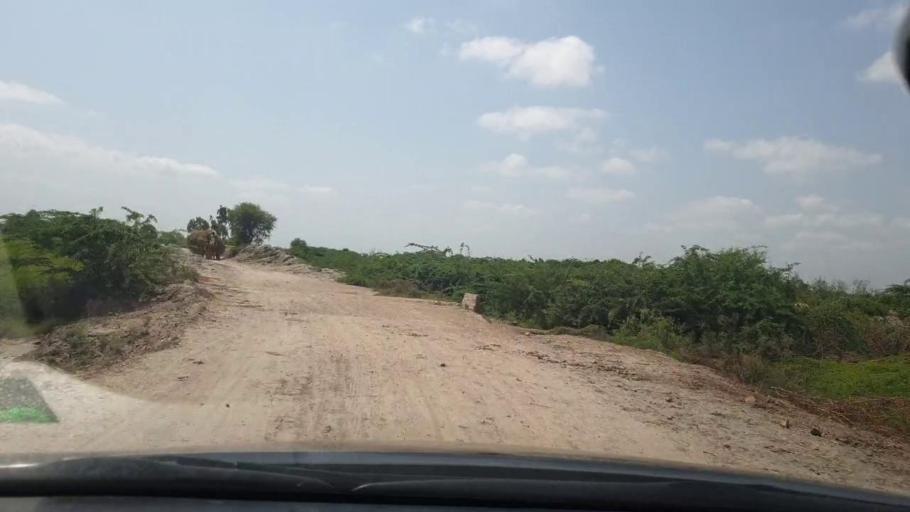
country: PK
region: Sindh
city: Tando Bago
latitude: 24.8517
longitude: 69.0909
